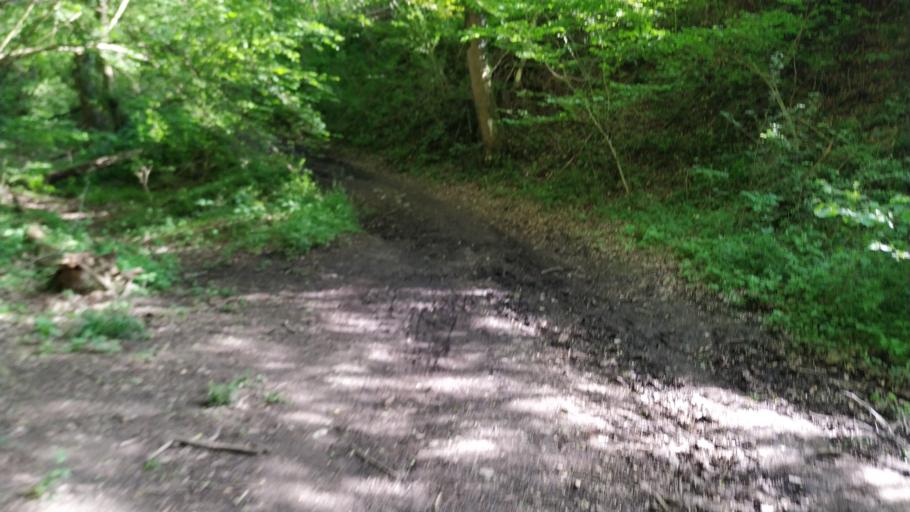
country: BE
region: Wallonia
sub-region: Province de Namur
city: Namur
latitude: 50.4795
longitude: 4.9291
